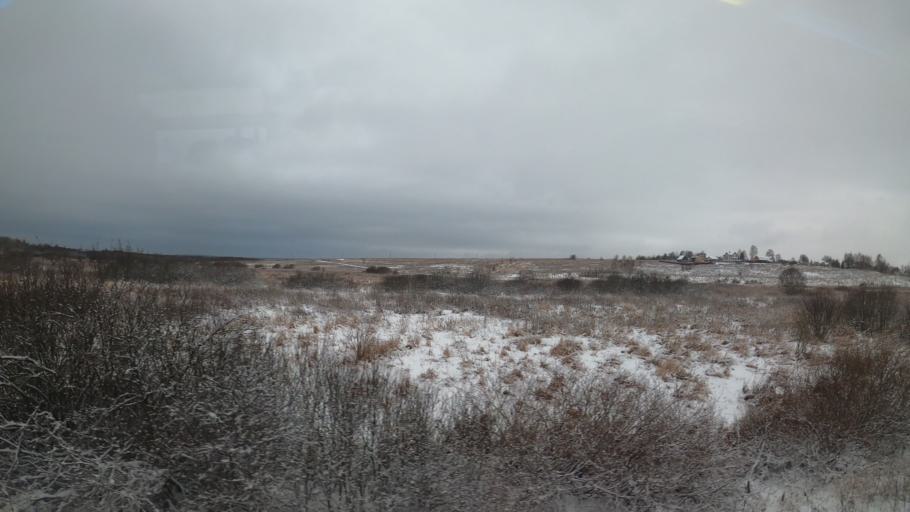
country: RU
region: Jaroslavl
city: Pereslavl'-Zalesskiy
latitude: 56.6985
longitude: 38.9157
